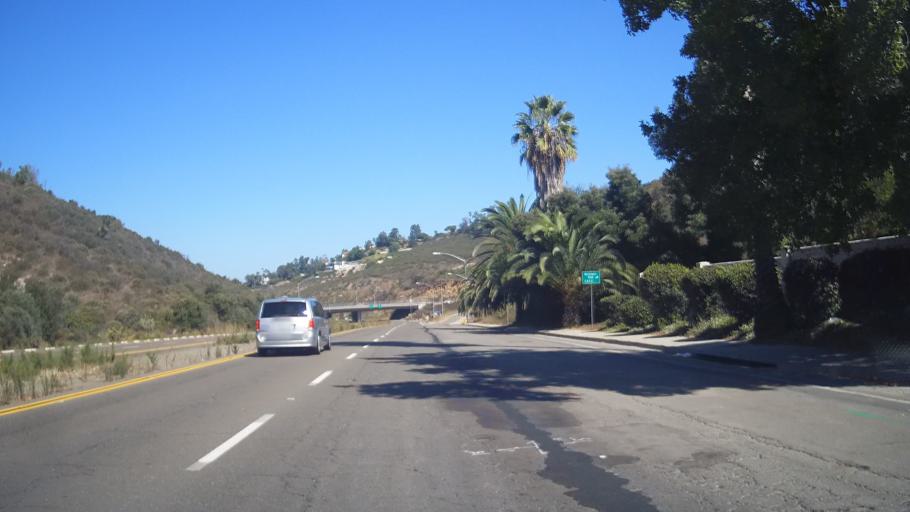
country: US
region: California
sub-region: San Diego County
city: Lemon Grove
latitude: 32.7688
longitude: -117.0968
